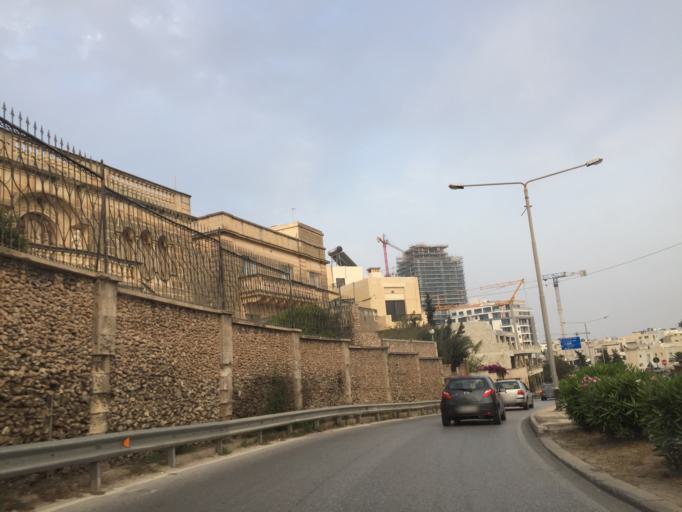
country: MT
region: Is-Swieqi
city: Swieqi
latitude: 35.9237
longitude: 14.4851
